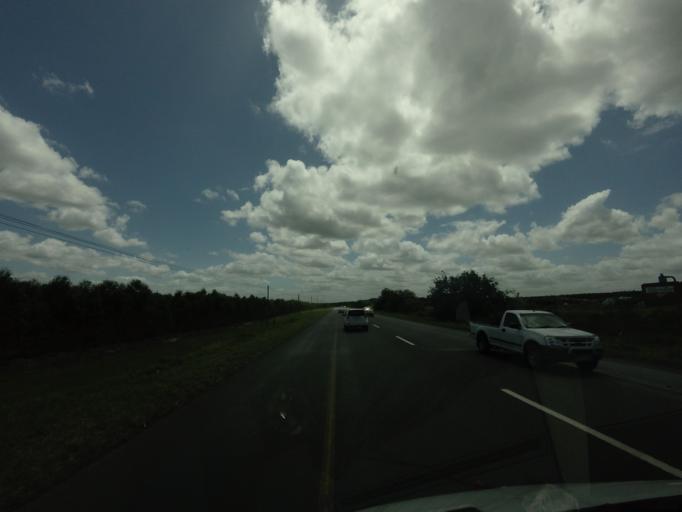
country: ZA
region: KwaZulu-Natal
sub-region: uThungulu District Municipality
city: KwaMbonambi
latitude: -28.5737
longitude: 32.1078
